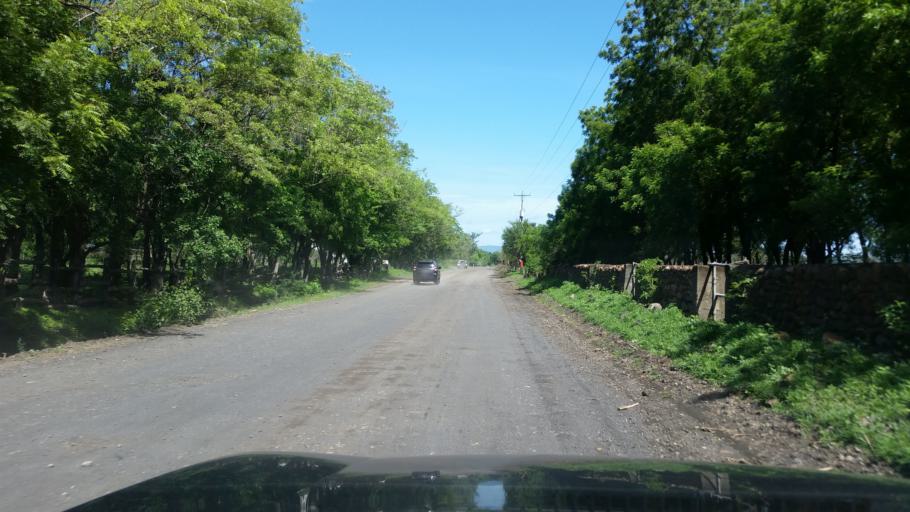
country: NI
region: Chinandega
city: Puerto Morazan
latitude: 12.7691
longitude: -87.0723
